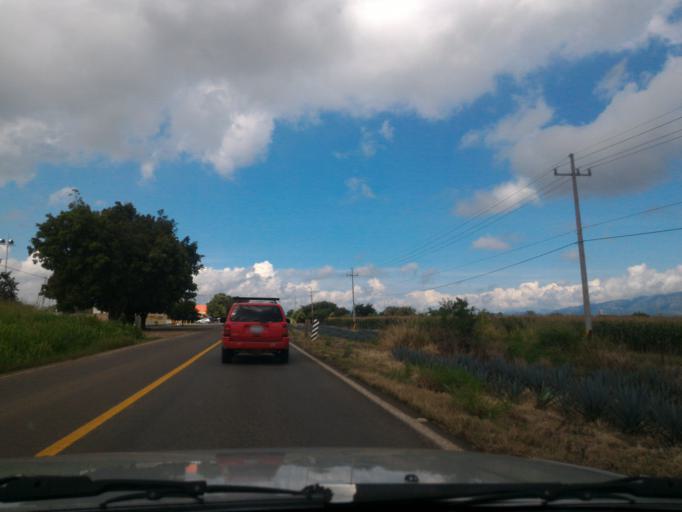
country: MX
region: Jalisco
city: Amatitan
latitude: 20.8549
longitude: -103.7626
